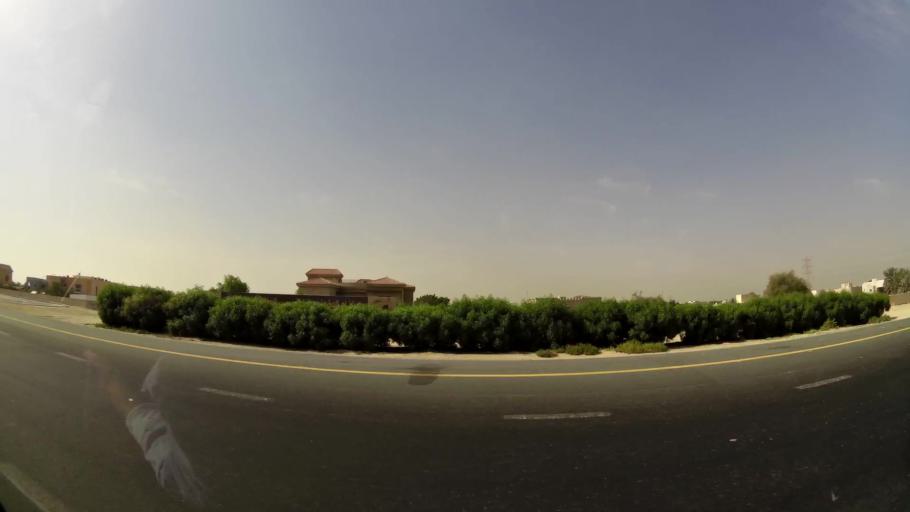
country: AE
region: Ash Shariqah
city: Sharjah
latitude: 25.2519
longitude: 55.4088
